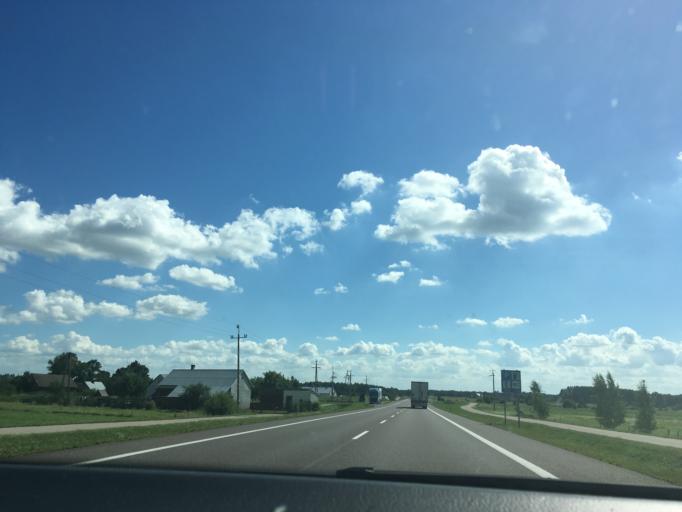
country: PL
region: Podlasie
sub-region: Powiat sokolski
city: Suchowola
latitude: 53.7106
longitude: 23.0997
